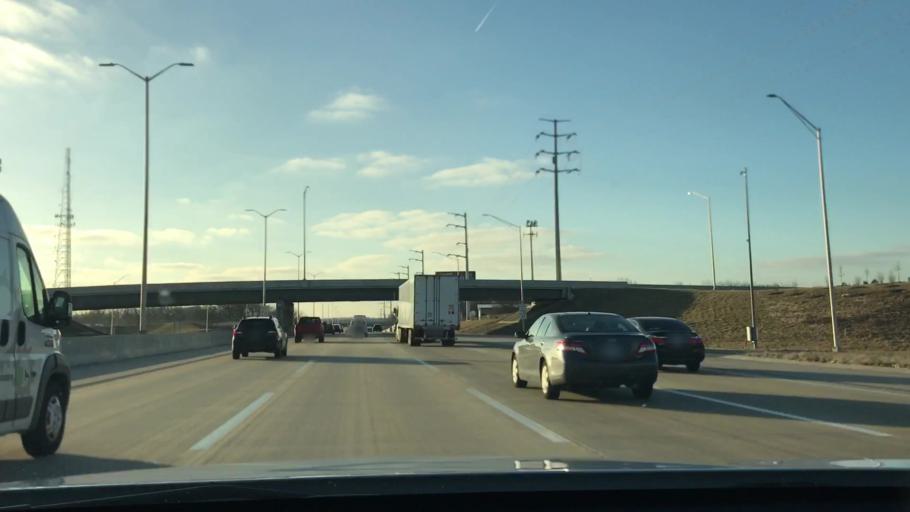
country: US
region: Illinois
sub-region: Kane County
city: East Dundee
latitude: 42.0669
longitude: -88.2571
